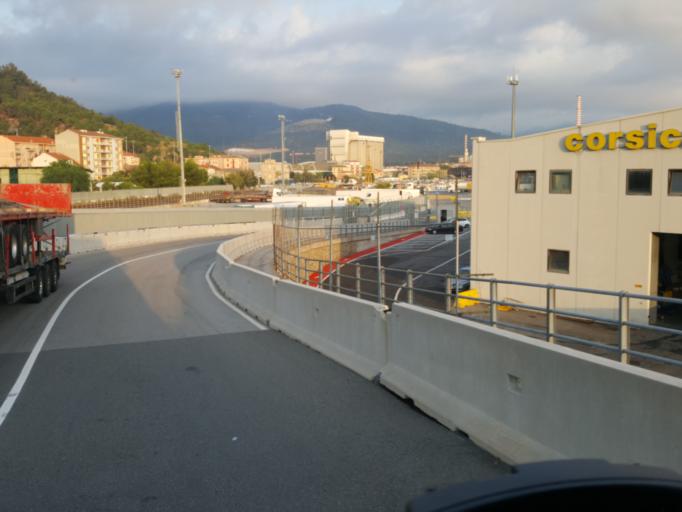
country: IT
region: Liguria
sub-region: Provincia di Savona
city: Bergeggi
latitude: 44.2625
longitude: 8.4491
